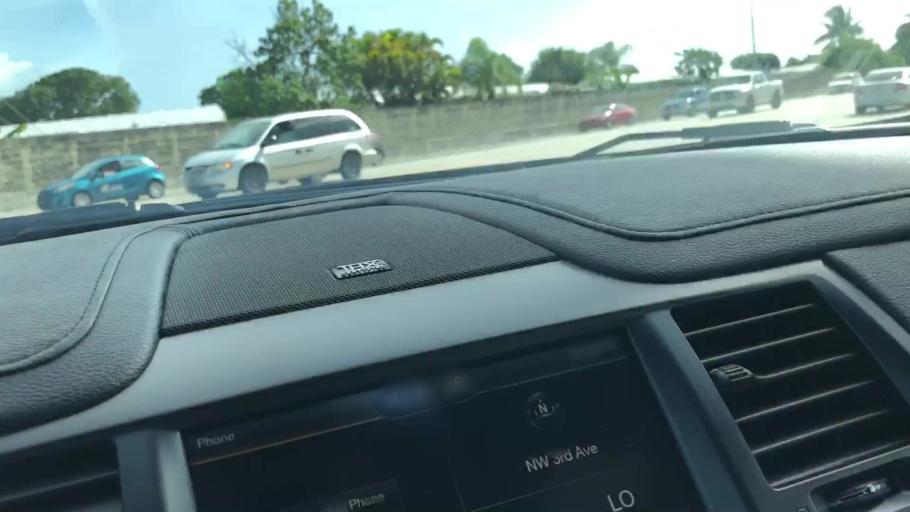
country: US
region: Florida
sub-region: Broward County
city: Kendall Green
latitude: 26.2603
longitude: -80.1273
